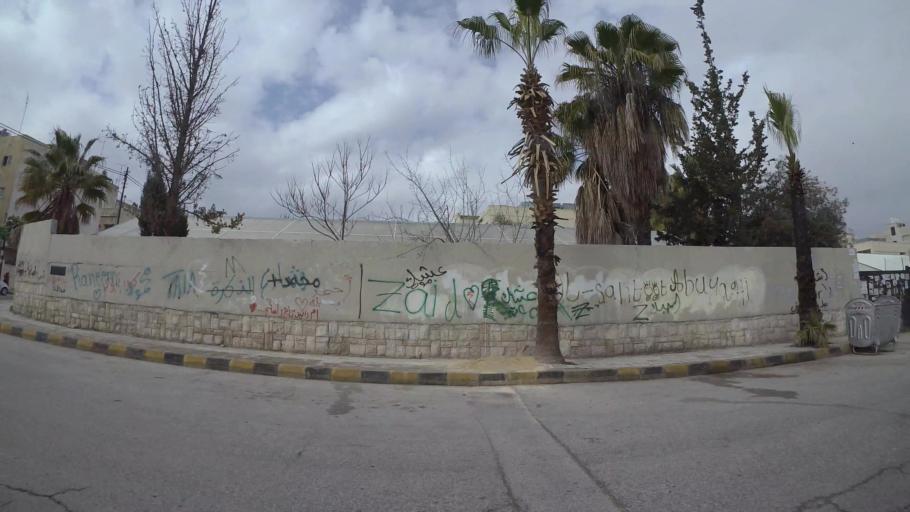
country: JO
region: Amman
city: Amman
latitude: 31.9701
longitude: 35.9347
